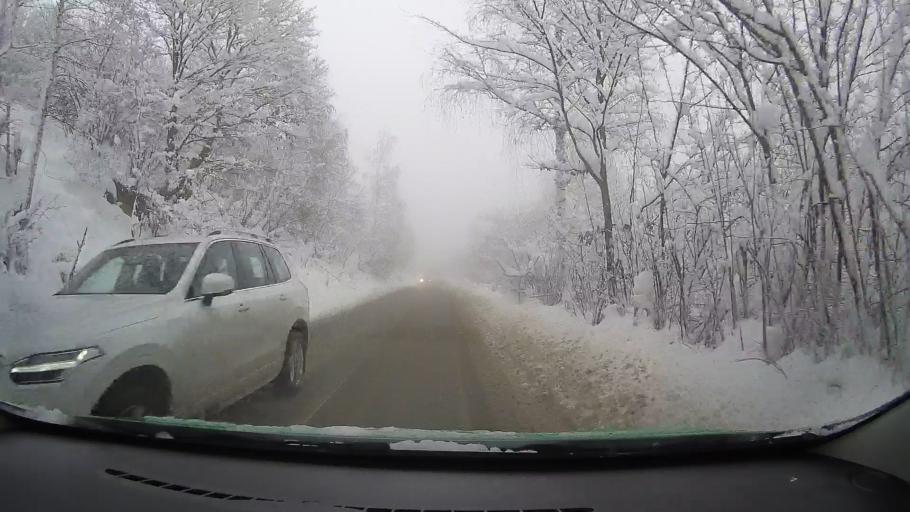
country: RO
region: Sibiu
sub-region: Comuna Poiana Sibiului
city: Poiana Sibiului
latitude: 45.7978
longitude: 23.7852
